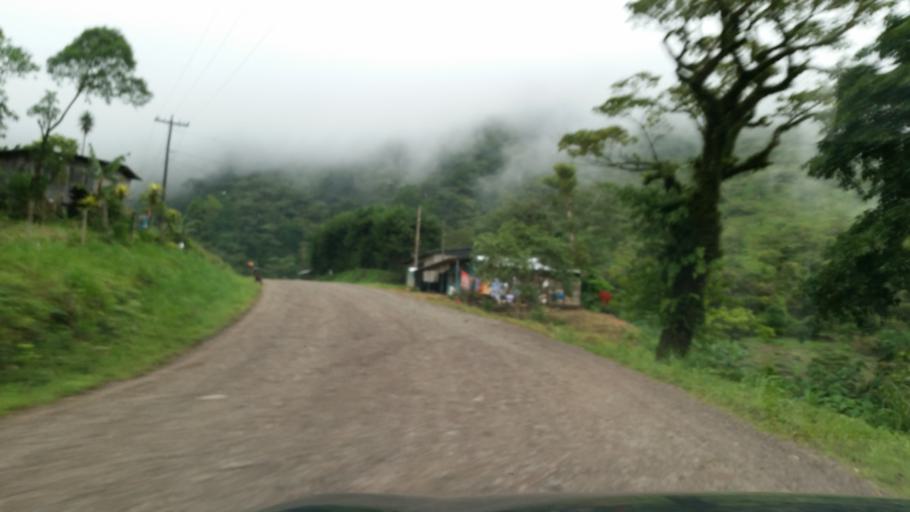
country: NI
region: Jinotega
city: San Jose de Bocay
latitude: 13.2820
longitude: -85.7176
